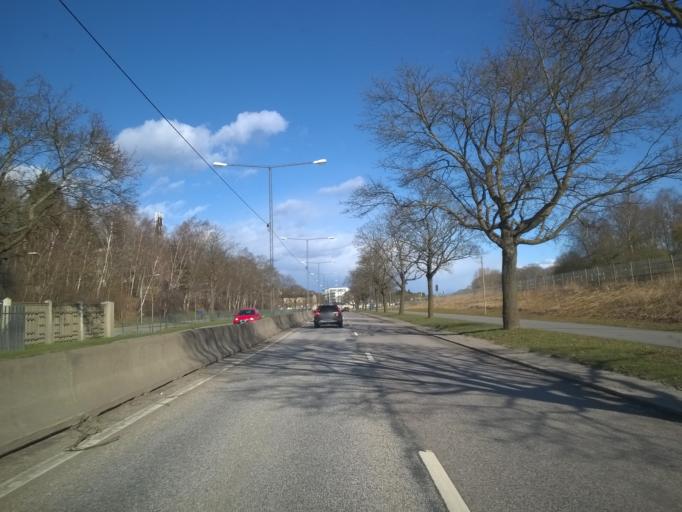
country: SE
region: Stockholm
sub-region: Stockholms Kommun
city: Bromma
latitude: 59.3424
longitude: 17.9191
